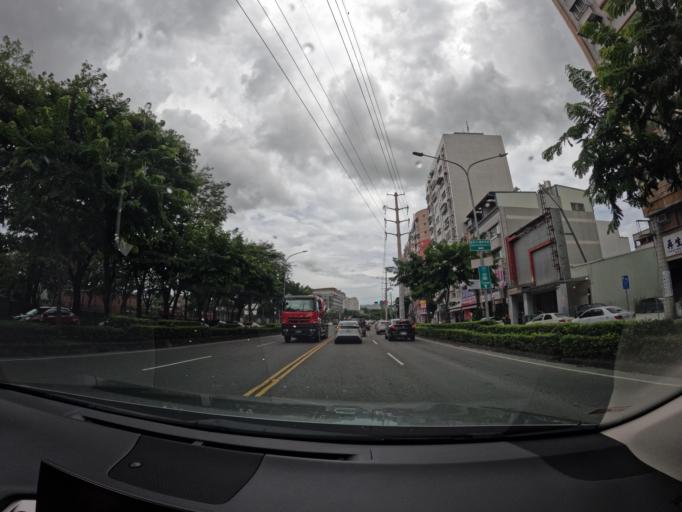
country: TW
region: Kaohsiung
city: Kaohsiung
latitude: 22.7271
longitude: 120.3111
